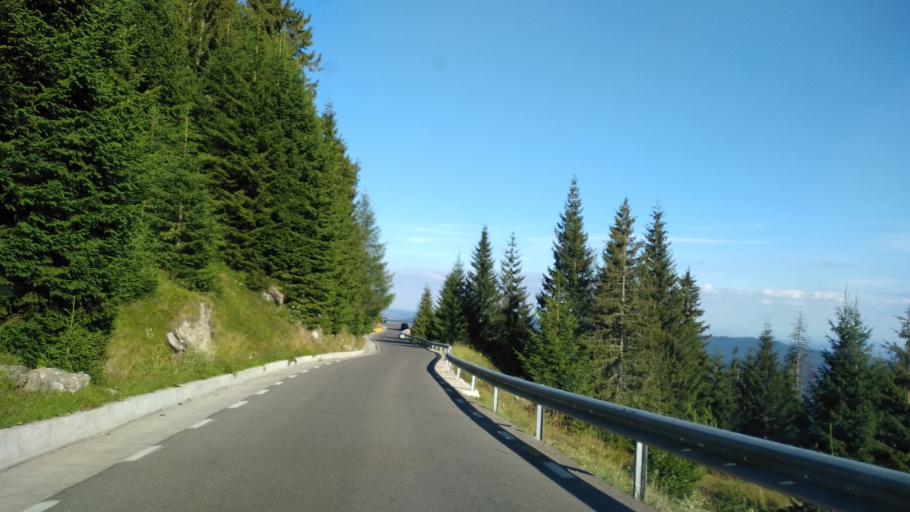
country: RO
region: Dambovita
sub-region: Comuna Moroeni
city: Glod
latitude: 45.3222
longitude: 25.4706
